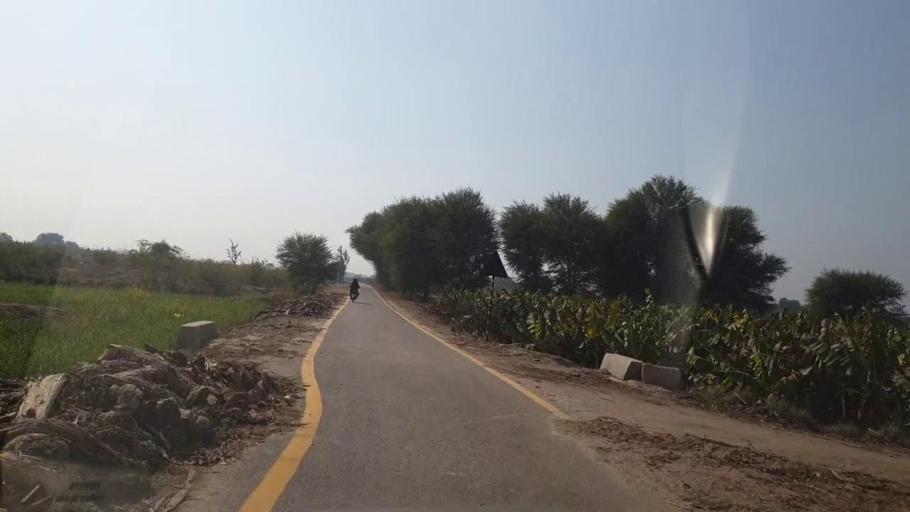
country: PK
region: Sindh
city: Matiari
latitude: 25.5369
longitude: 68.4938
